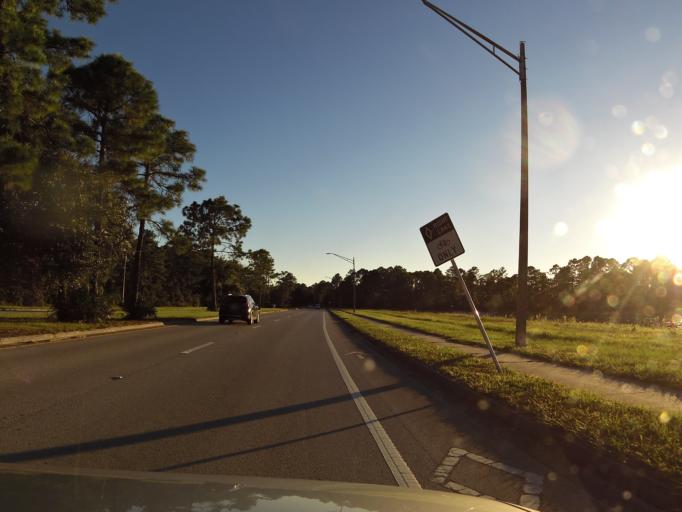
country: US
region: Florida
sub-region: Duval County
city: Jacksonville Beach
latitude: 30.2832
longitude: -81.4384
